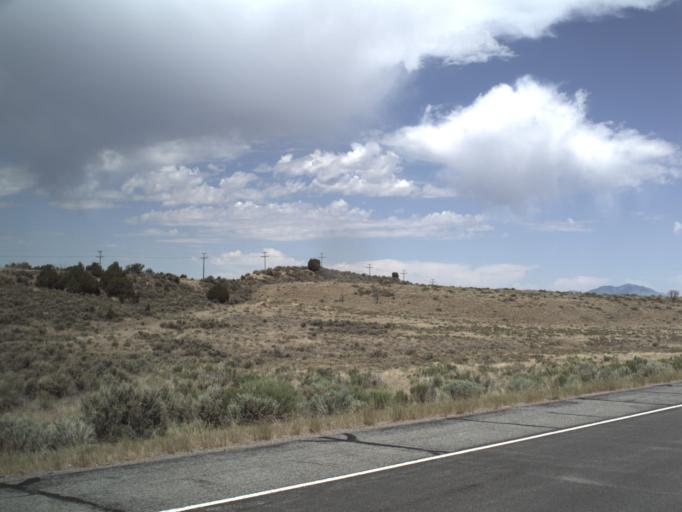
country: US
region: Utah
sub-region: Utah County
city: Genola
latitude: 39.9738
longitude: -112.2582
